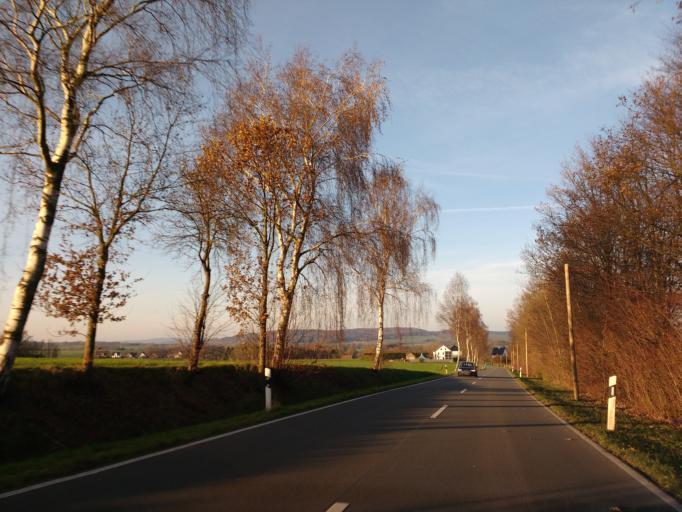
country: DE
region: North Rhine-Westphalia
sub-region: Regierungsbezirk Detmold
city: Blomberg
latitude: 51.9145
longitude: 9.0832
